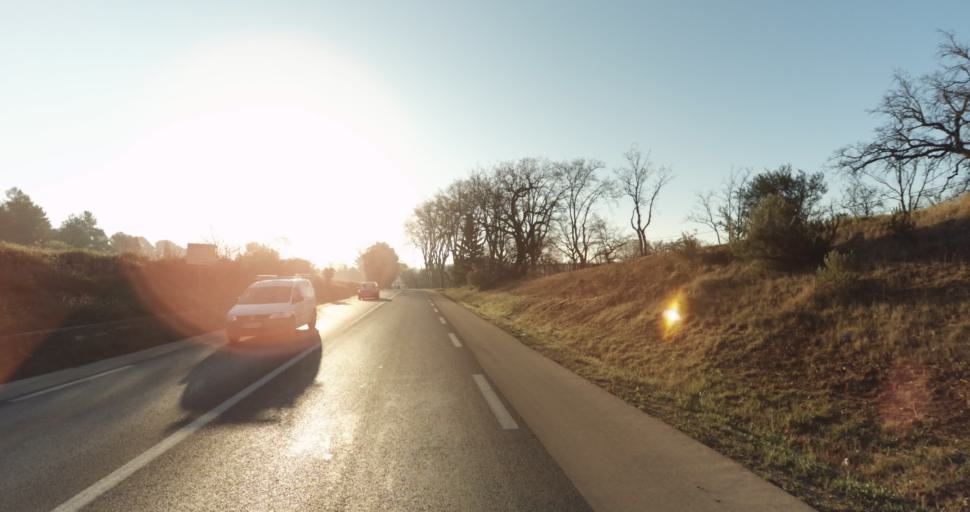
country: FR
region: Provence-Alpes-Cote d'Azur
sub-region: Departement des Bouches-du-Rhone
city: Eguilles
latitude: 43.5365
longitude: 5.3873
